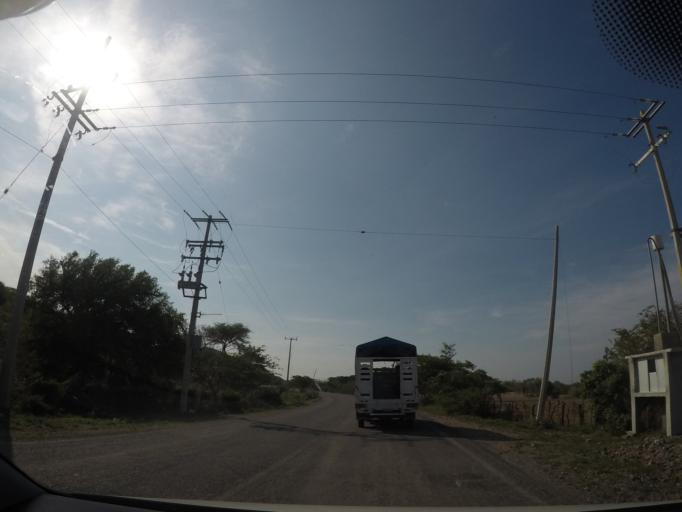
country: MX
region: Oaxaca
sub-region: Salina Cruz
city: Salina Cruz
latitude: 16.2328
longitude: -95.1493
